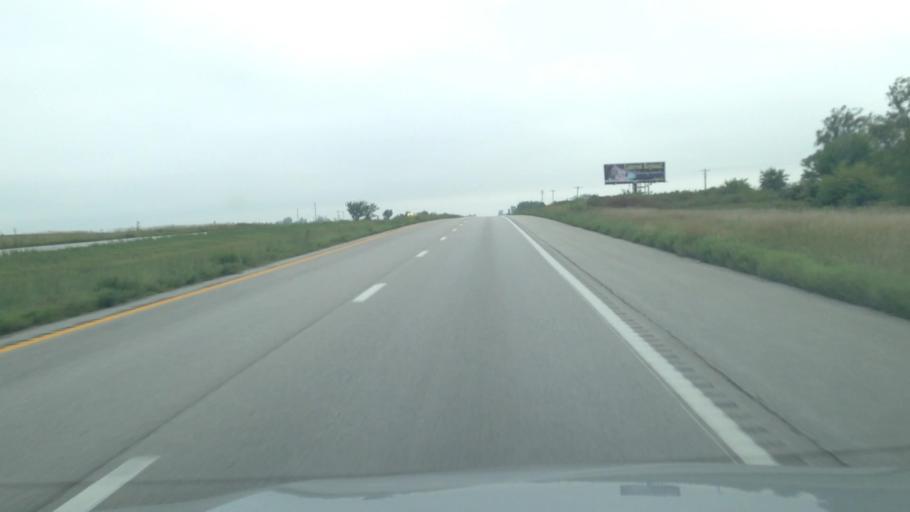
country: US
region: Missouri
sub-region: Clinton County
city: Cameron
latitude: 39.8356
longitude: -94.1849
